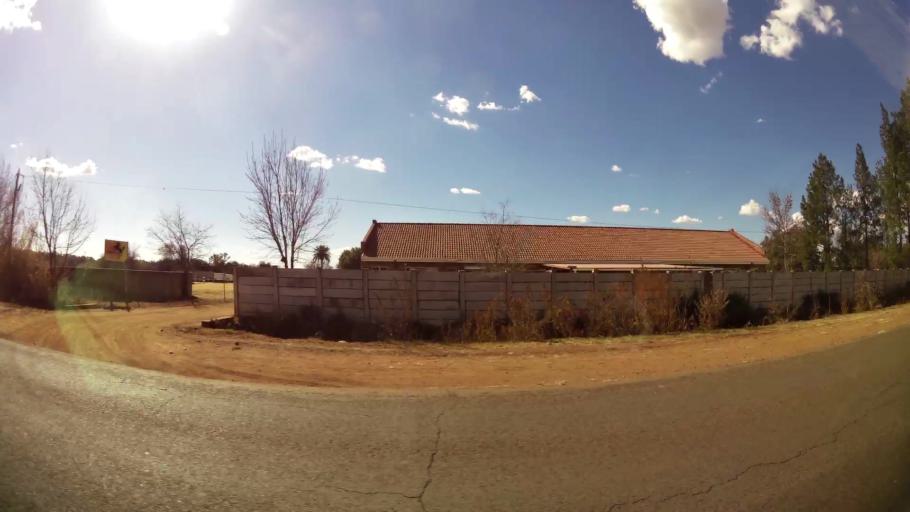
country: ZA
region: North-West
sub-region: Dr Kenneth Kaunda District Municipality
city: Klerksdorp
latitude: -26.8578
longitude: 26.6219
